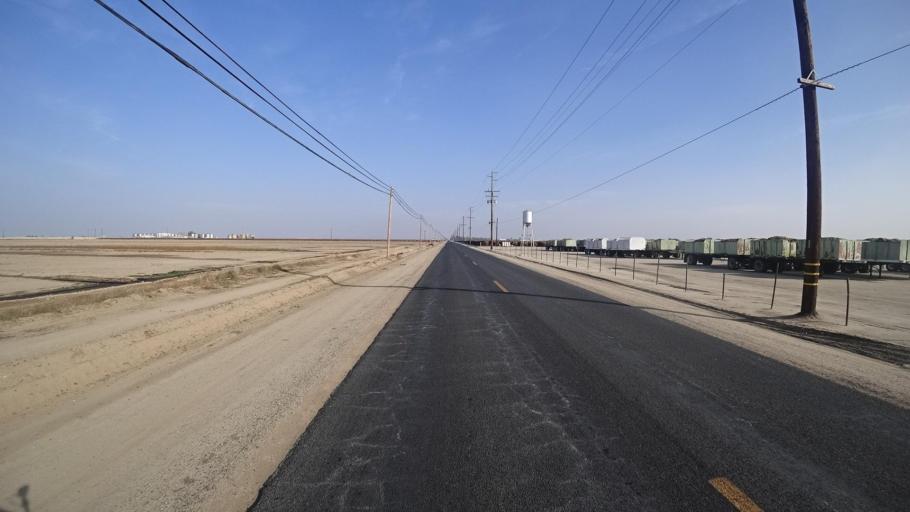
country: US
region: California
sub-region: Kern County
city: Delano
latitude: 35.7760
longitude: -119.1998
